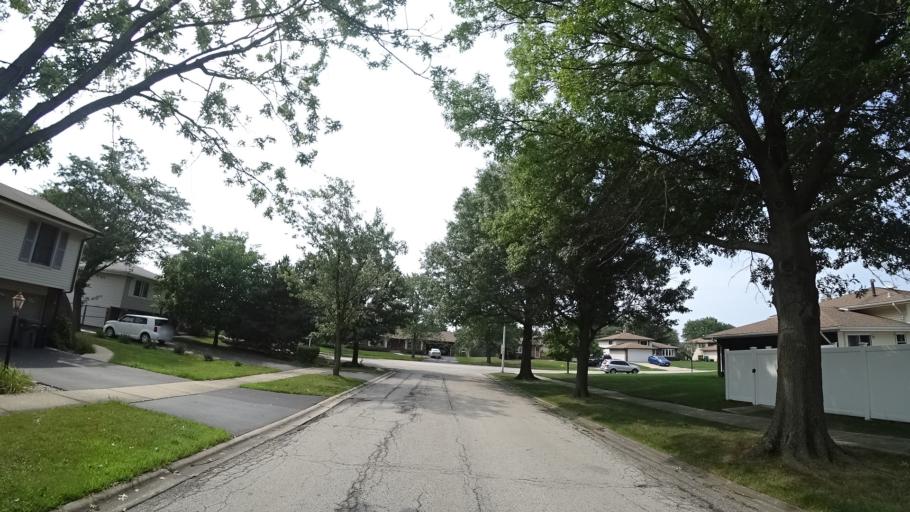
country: US
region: Illinois
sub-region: Cook County
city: Orland Park
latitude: 41.6168
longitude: -87.8589
